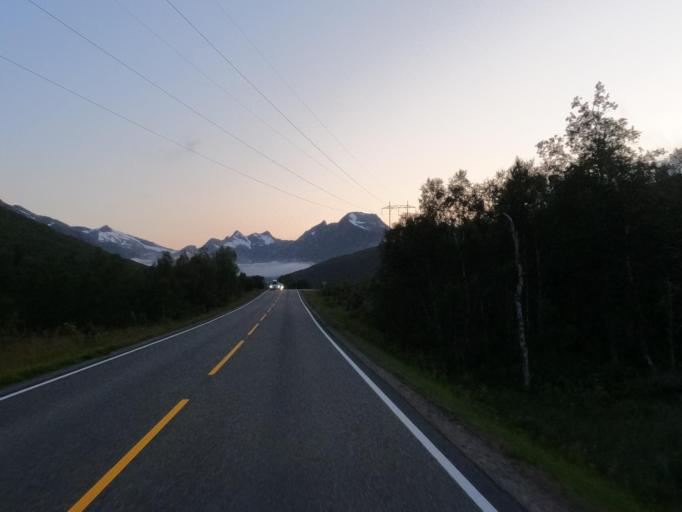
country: NO
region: Nordland
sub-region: Lodingen
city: Lodingen
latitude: 68.5270
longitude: 15.8278
